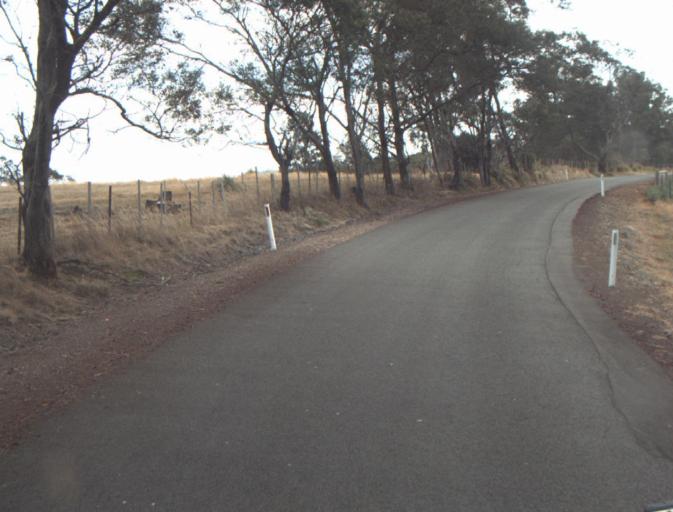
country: AU
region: Tasmania
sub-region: Launceston
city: Mayfield
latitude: -41.2839
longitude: 147.0243
